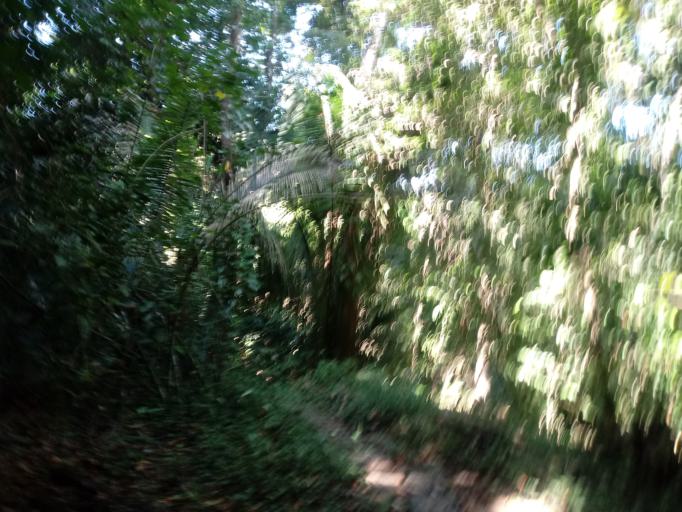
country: CR
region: Puntarenas
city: Paquera
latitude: 9.5868
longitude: -85.0961
